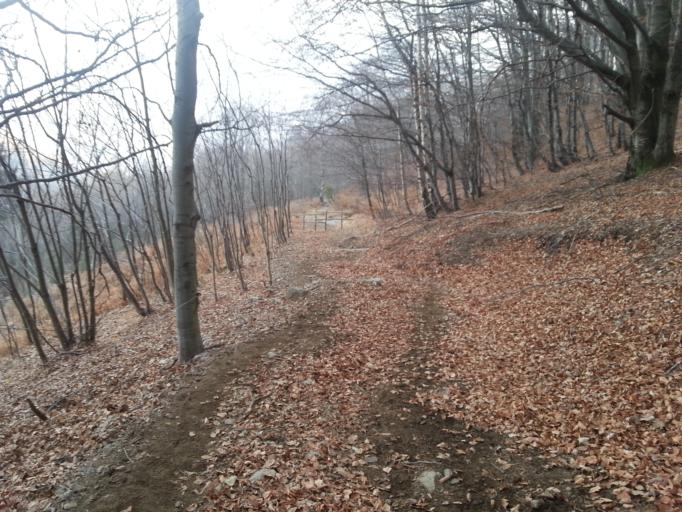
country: IT
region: Lombardy
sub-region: Provincia di Varese
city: Curiglia
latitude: 46.0317
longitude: 8.8460
